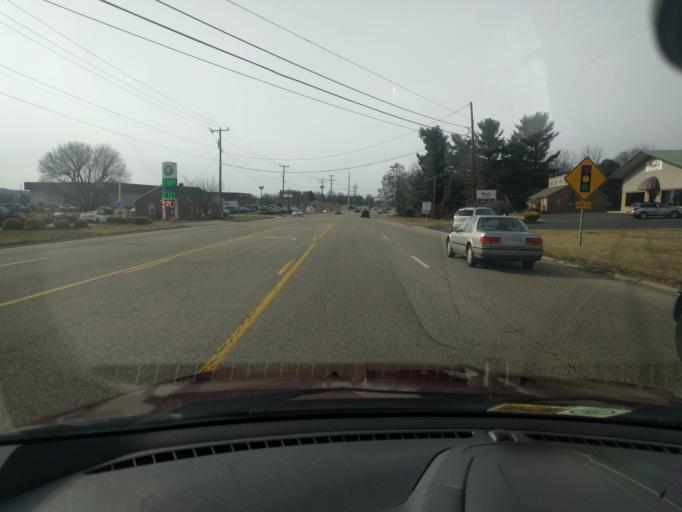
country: US
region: Virginia
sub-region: Augusta County
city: Stuarts Draft
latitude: 38.0308
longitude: -79.0461
